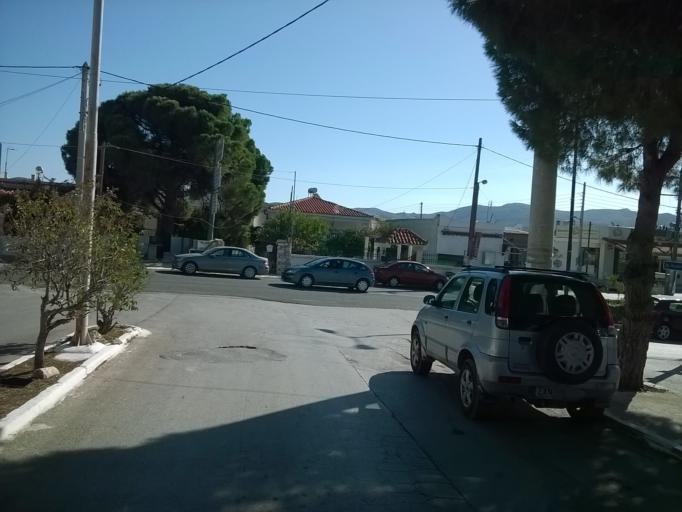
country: GR
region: Attica
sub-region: Nomarchia Anatolikis Attikis
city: Anavyssos
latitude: 37.7375
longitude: 23.9520
